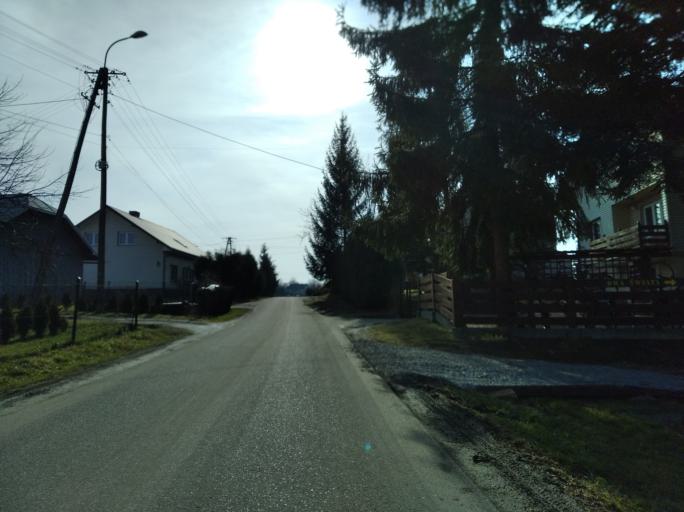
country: PL
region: Subcarpathian Voivodeship
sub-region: Powiat brzozowski
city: Humniska
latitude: 49.6664
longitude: 22.0536
